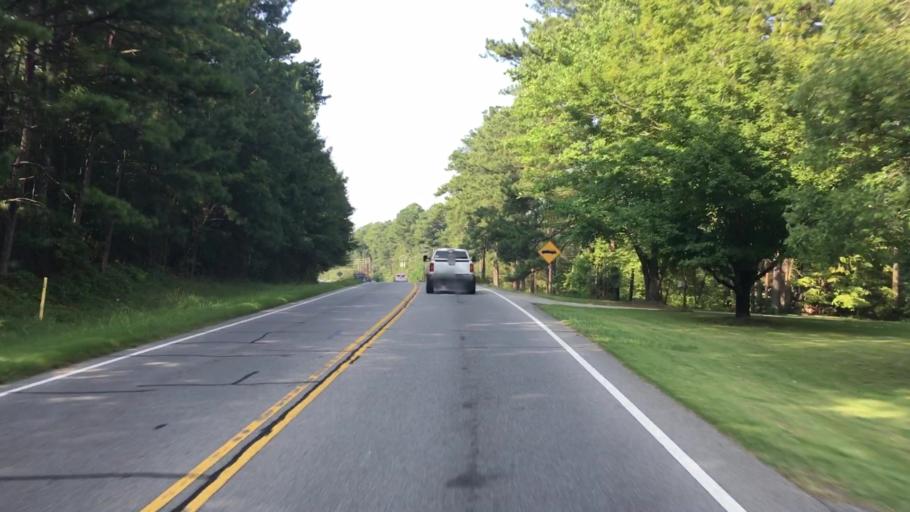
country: US
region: Georgia
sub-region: Barrow County
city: Russell
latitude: 33.9730
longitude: -83.7138
